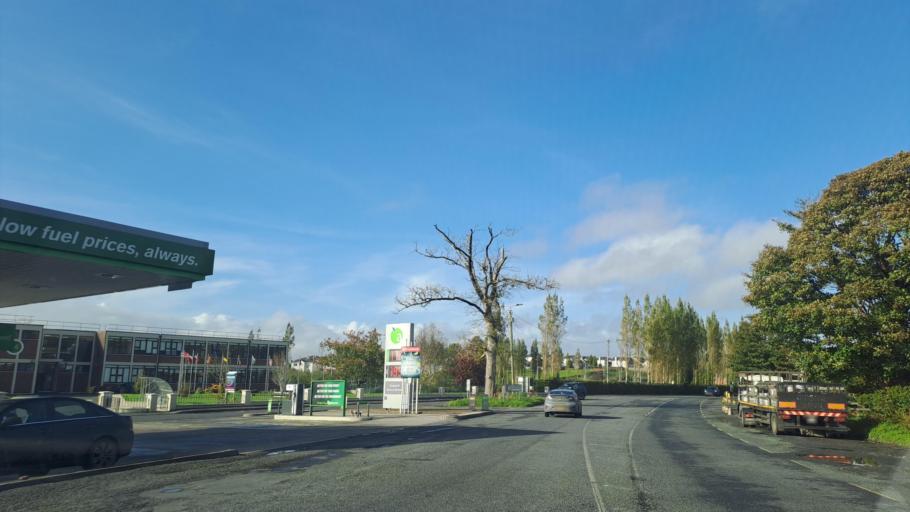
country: IE
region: Ulster
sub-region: An Cabhan
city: Cootehill
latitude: 54.0672
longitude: -7.0625
